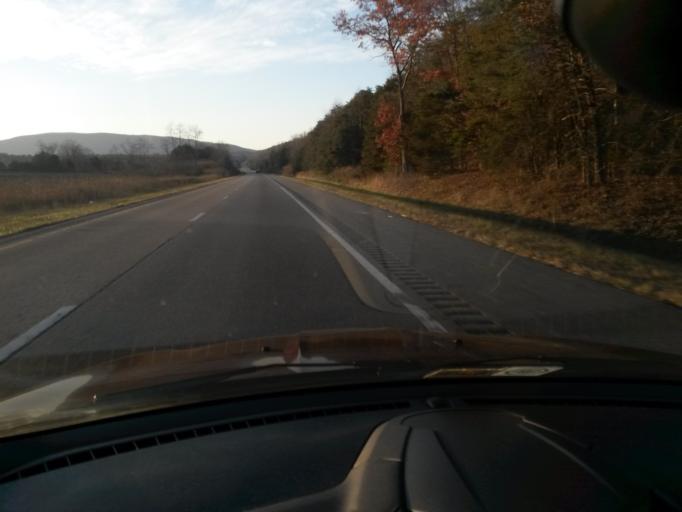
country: US
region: Virginia
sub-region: City of Lexington
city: Lexington
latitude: 37.8685
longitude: -79.5057
